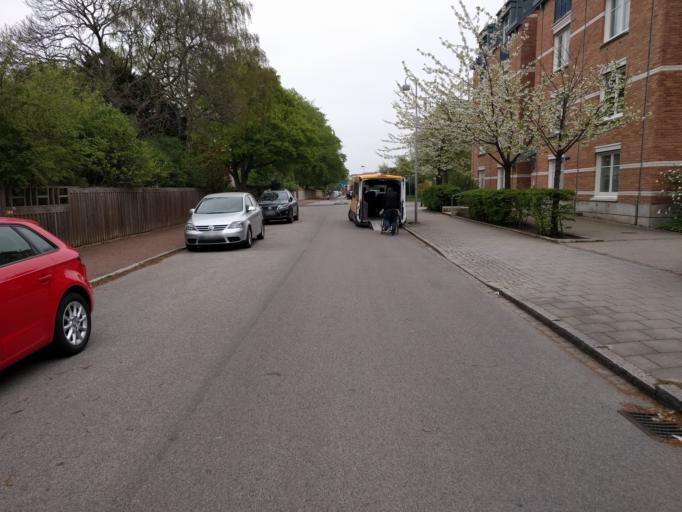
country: SE
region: Skane
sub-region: Malmo
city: Malmoe
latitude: 55.5965
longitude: 12.9617
